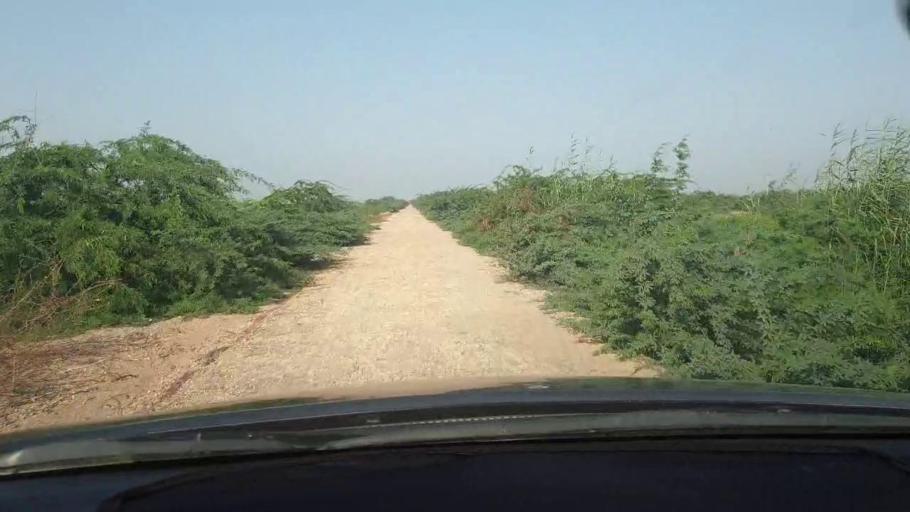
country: PK
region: Sindh
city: Tando Bago
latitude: 24.6799
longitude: 69.1635
